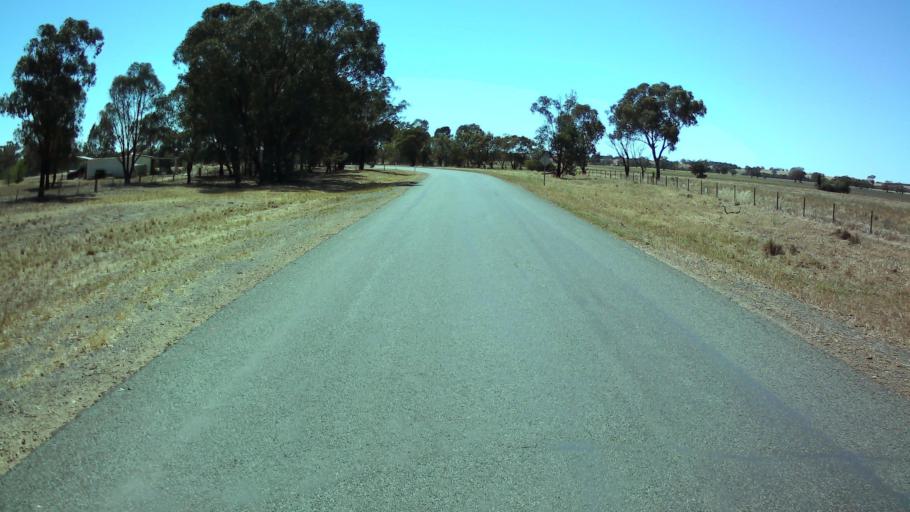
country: AU
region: New South Wales
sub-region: Weddin
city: Grenfell
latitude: -34.0023
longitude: 148.3837
